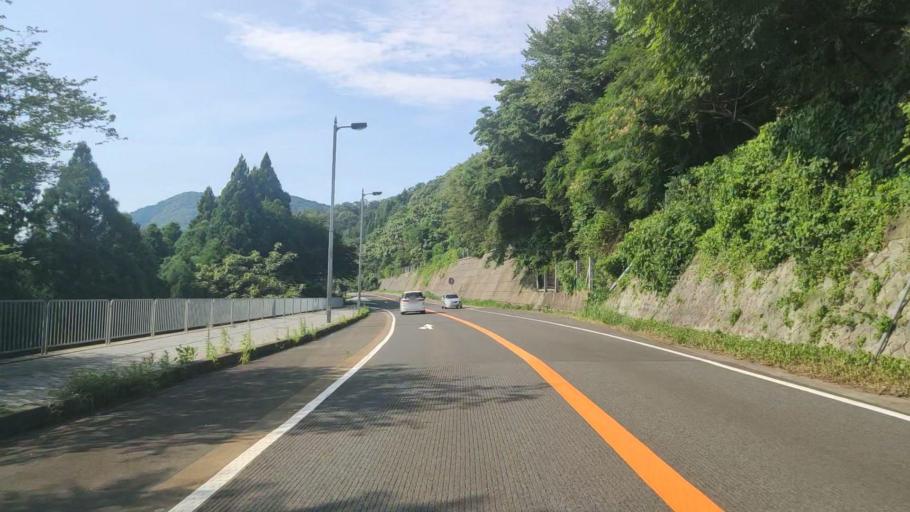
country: JP
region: Fukui
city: Takefu
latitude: 35.7948
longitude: 136.0928
